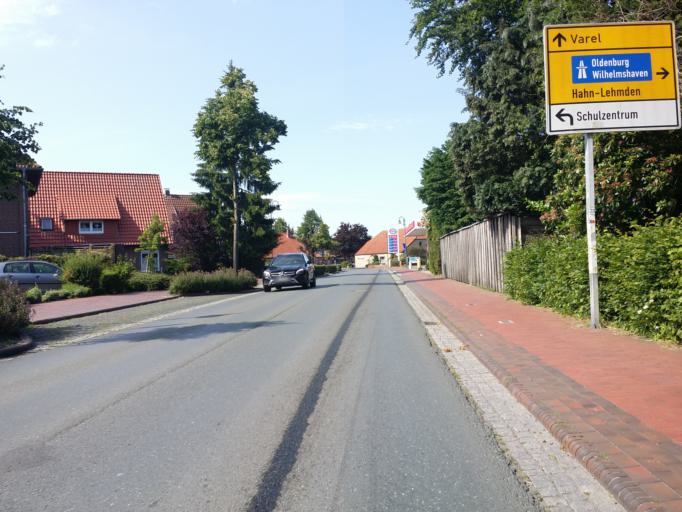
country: DE
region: Lower Saxony
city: Wiefelstede
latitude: 53.2581
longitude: 8.1154
